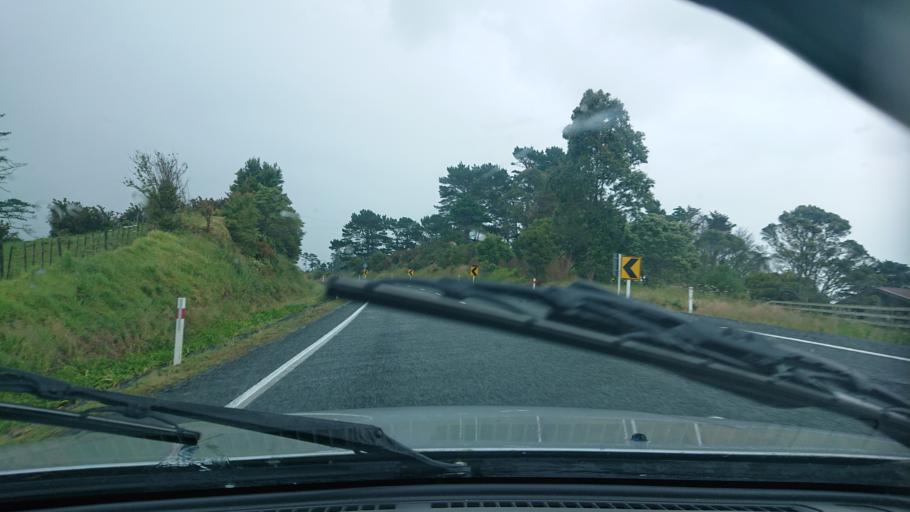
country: NZ
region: Auckland
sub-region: Auckland
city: Wellsford
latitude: -36.3320
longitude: 174.4688
